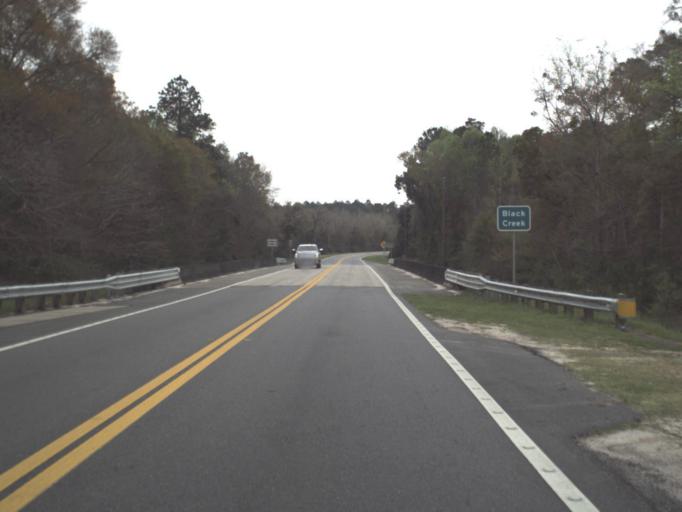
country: US
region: Florida
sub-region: Gulf County
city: Wewahitchka
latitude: 30.0267
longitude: -84.9823
